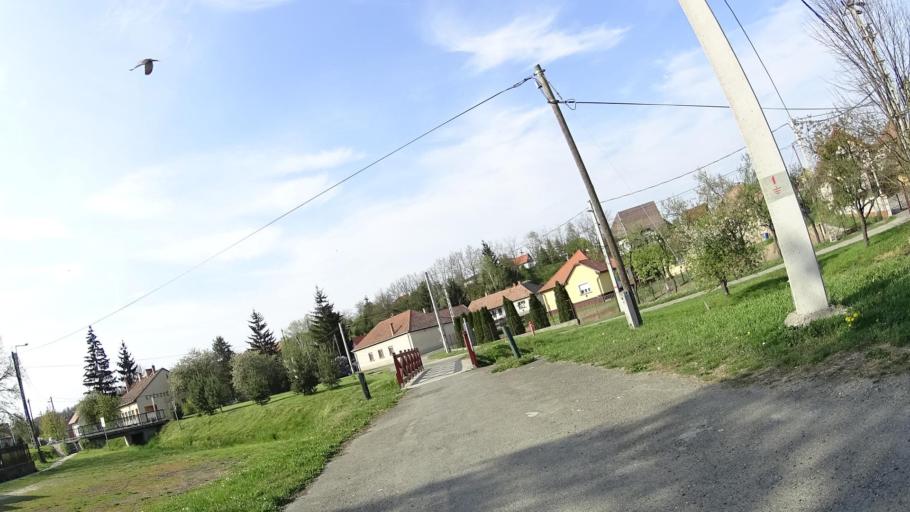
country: HU
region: Nograd
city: Retsag
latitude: 47.8874
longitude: 19.1962
